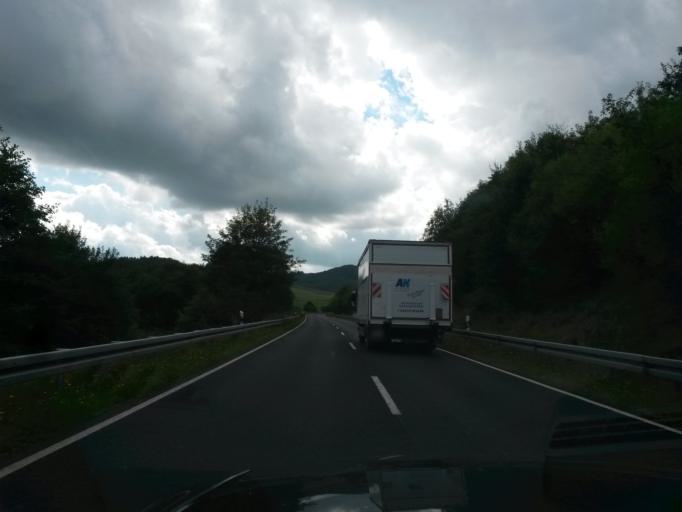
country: DE
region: Hesse
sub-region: Regierungsbezirk Kassel
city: Hilders
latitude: 50.5315
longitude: 9.9512
